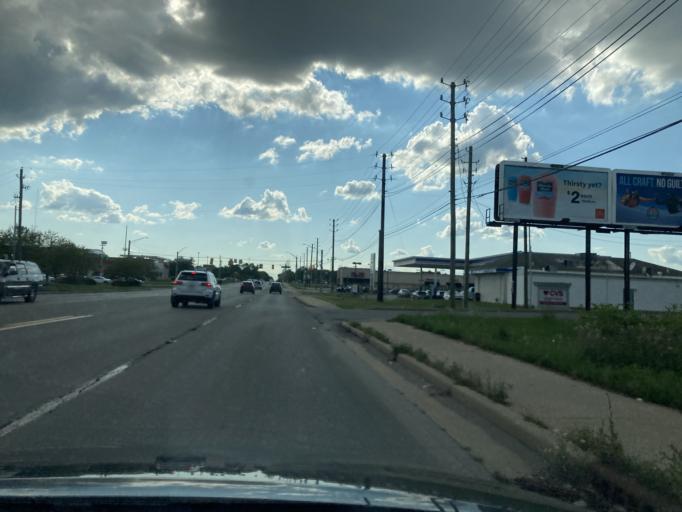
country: US
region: Indiana
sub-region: Marion County
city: Speedway
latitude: 39.8534
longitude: -86.2384
